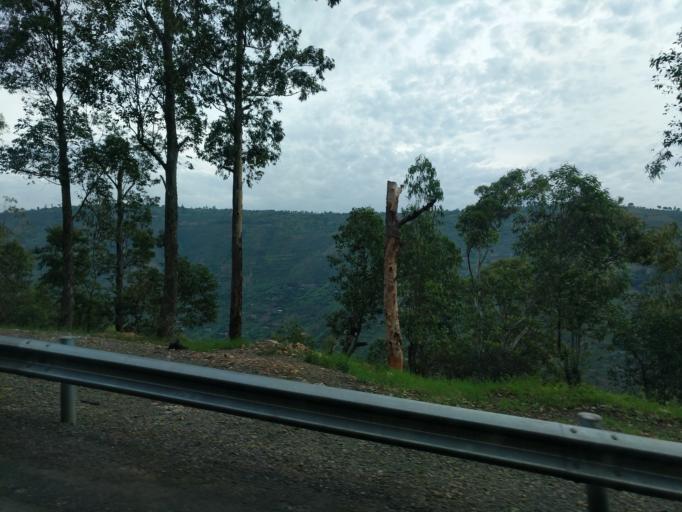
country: RW
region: Kigali
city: Kigali
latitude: -1.9367
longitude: 30.0274
